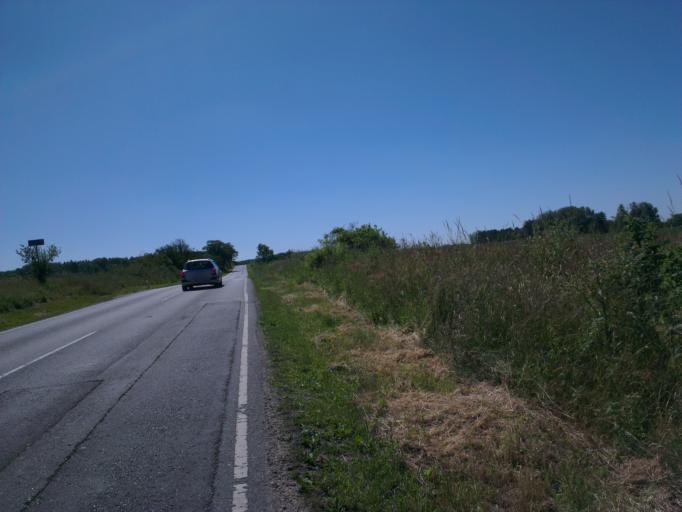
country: DK
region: Capital Region
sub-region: Frederikssund Kommune
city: Jaegerspris
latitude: 55.8717
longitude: 11.9603
